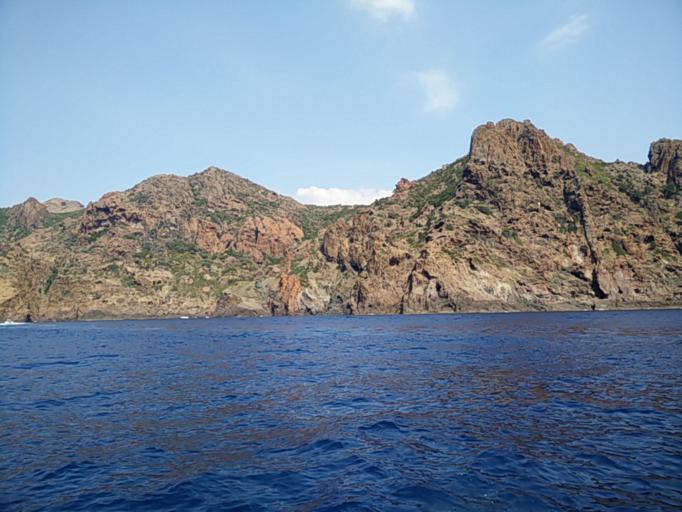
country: FR
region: Corsica
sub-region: Departement de la Corse-du-Sud
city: Cargese
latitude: 42.3382
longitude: 8.5504
